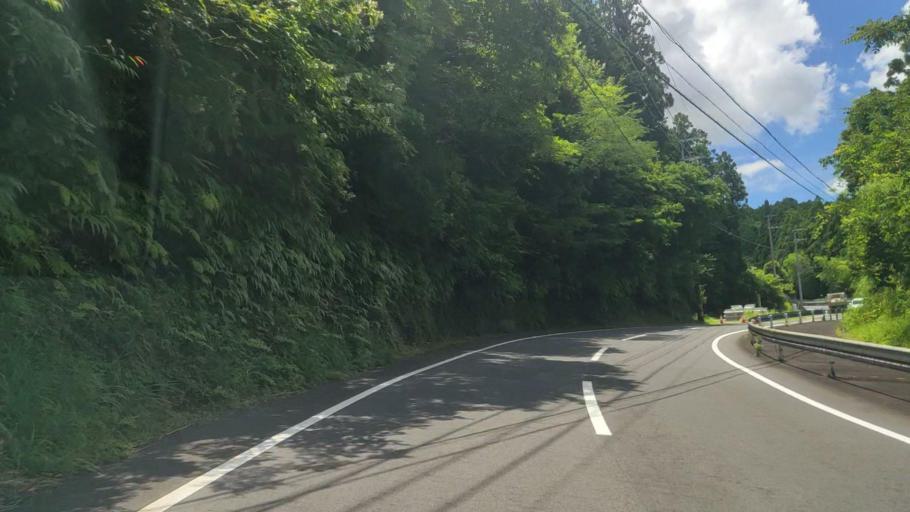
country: JP
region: Mie
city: Owase
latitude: 33.9533
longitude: 136.0691
